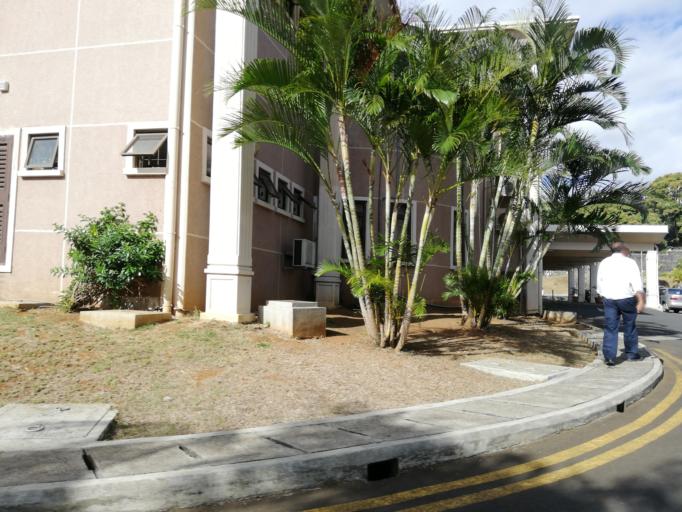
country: MU
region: Plaines Wilhems
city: Ebene
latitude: -20.2293
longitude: 57.4604
